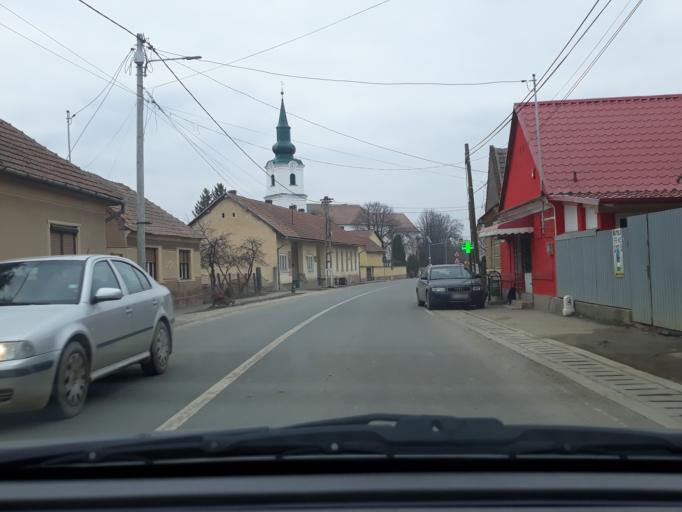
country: RO
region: Salaj
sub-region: Comuna Nusfalau
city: Nusfalau
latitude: 47.1955
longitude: 22.7014
